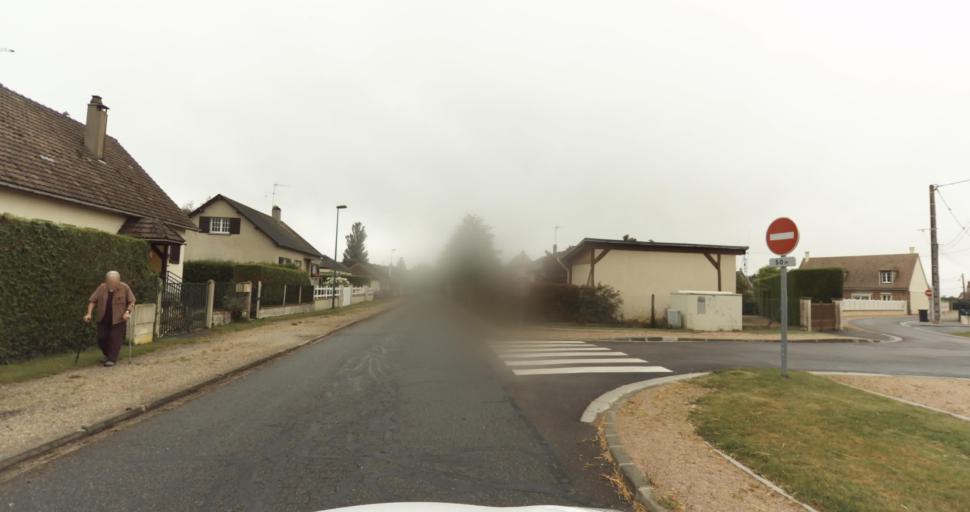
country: FR
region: Haute-Normandie
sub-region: Departement de l'Eure
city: Normanville
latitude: 49.0945
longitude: 1.1601
